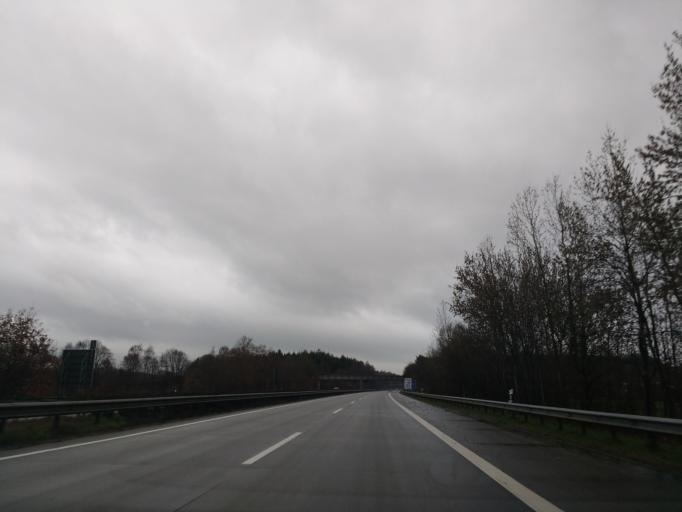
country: DE
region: Lower Saxony
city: Langen
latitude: 53.6171
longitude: 8.6634
